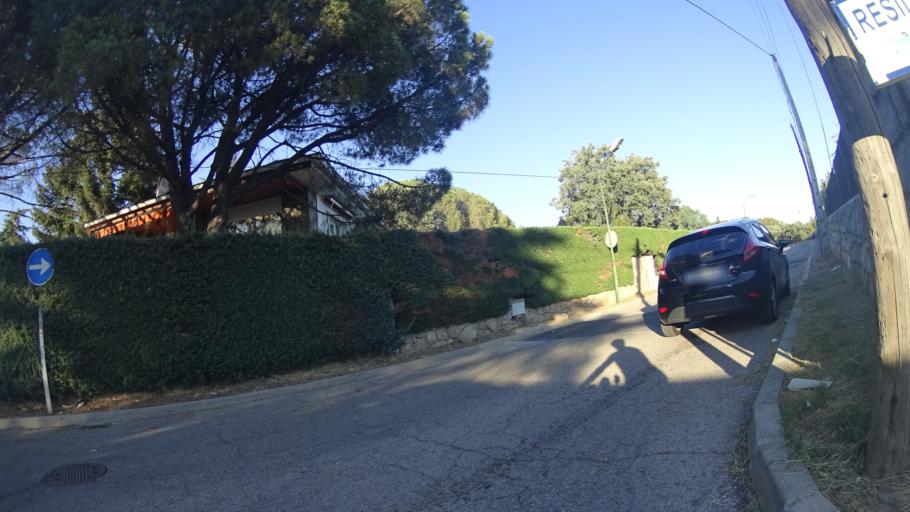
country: ES
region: Madrid
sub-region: Provincia de Madrid
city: Galapagar
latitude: 40.5665
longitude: -4.0019
